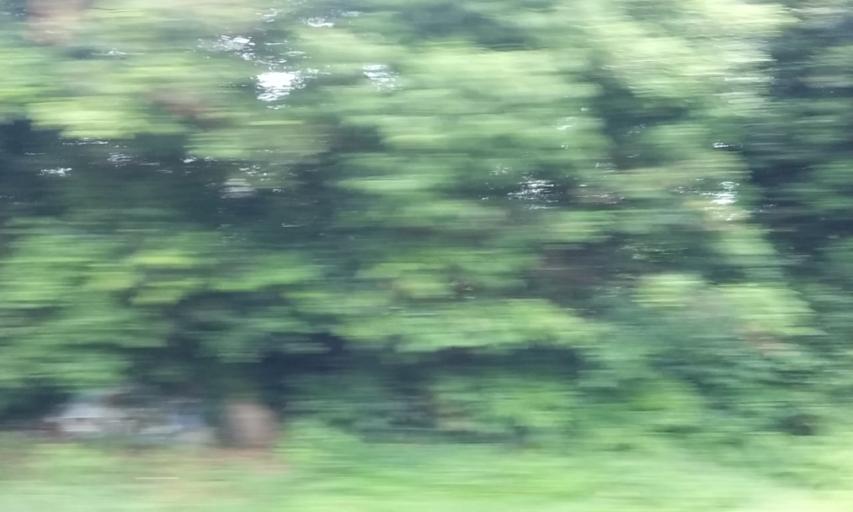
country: JP
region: Chiba
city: Katori-shi
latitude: 35.8936
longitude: 140.5133
